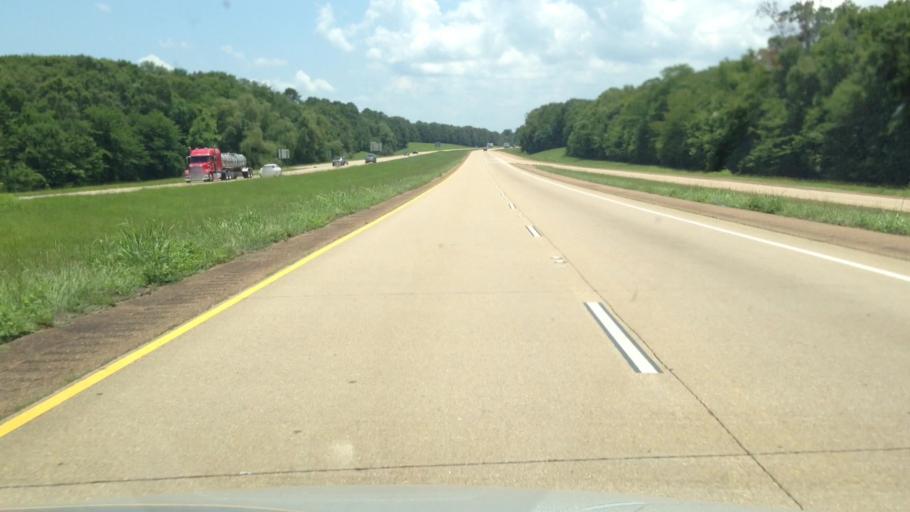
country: US
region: Louisiana
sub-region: Rapides Parish
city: Woodworth
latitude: 31.1610
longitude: -92.4579
